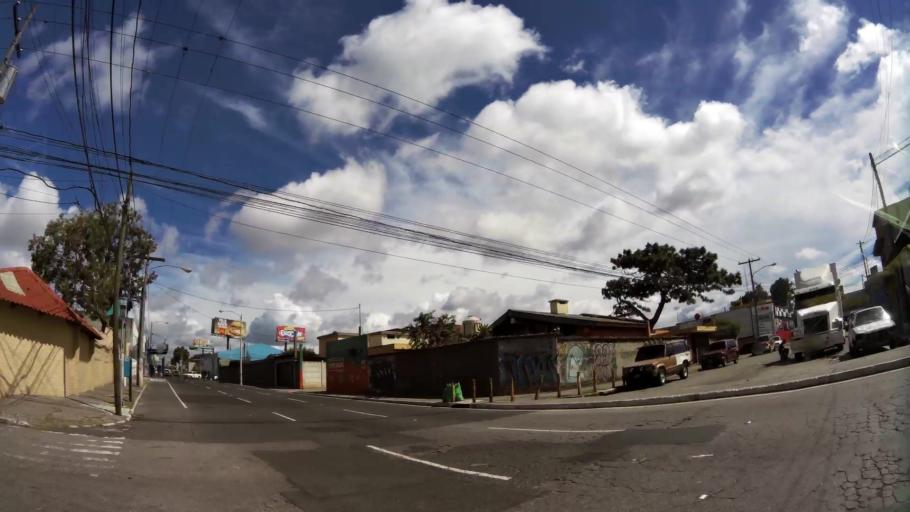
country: GT
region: Guatemala
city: Guatemala City
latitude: 14.5982
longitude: -90.5436
